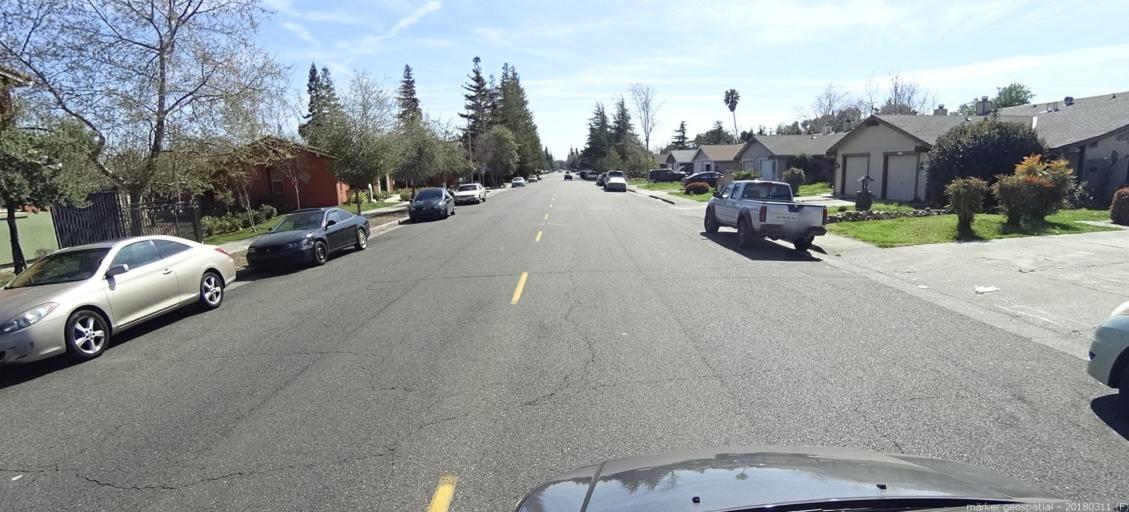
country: US
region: California
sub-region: Sacramento County
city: Parkway
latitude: 38.4941
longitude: -121.4344
